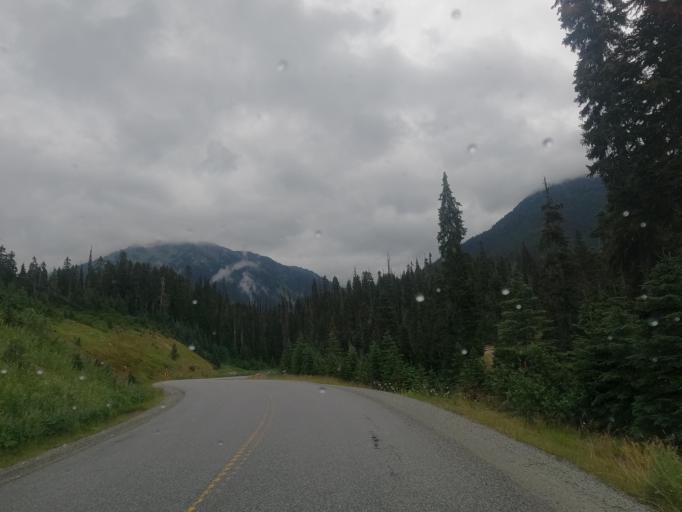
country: CA
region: British Columbia
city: Pemberton
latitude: 50.3835
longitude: -122.4695
